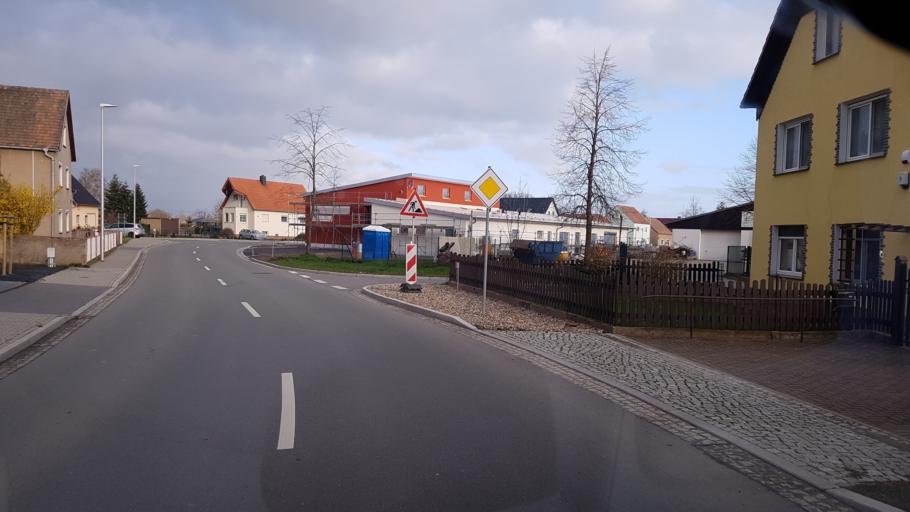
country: DE
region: Saxony
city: Nauwalde
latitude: 51.4173
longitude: 13.4103
